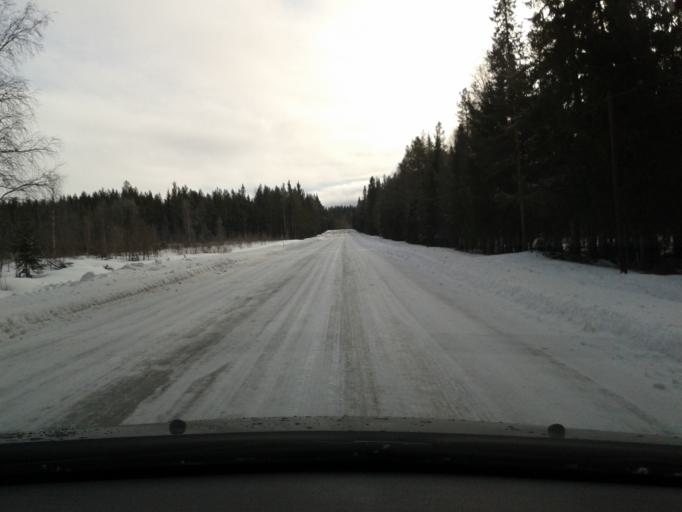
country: SE
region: Vaesterbotten
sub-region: Vilhelmina Kommun
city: Sjoberg
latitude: 64.7074
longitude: 16.2509
